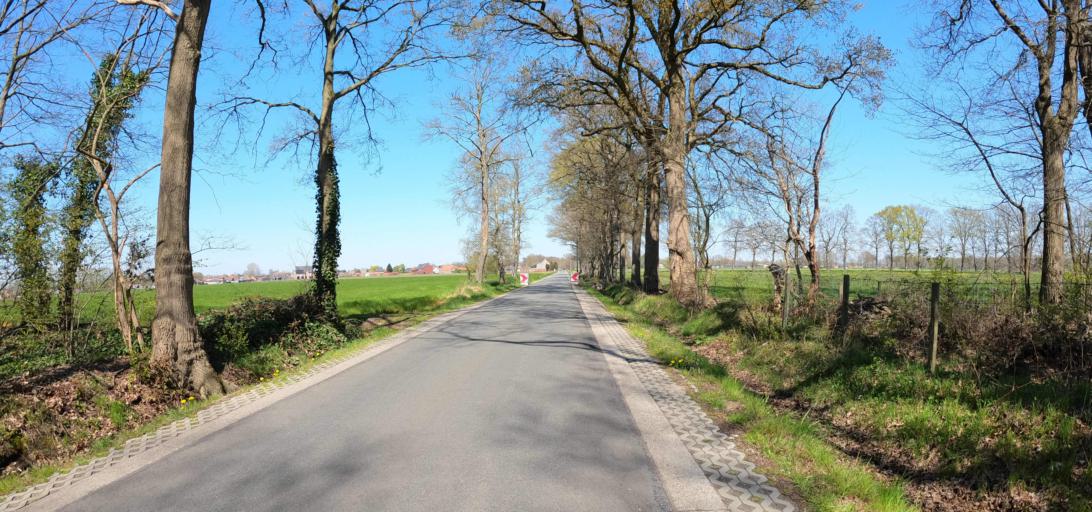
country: BE
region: Flanders
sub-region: Provincie Antwerpen
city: Oostmalle
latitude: 51.2948
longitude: 4.7489
